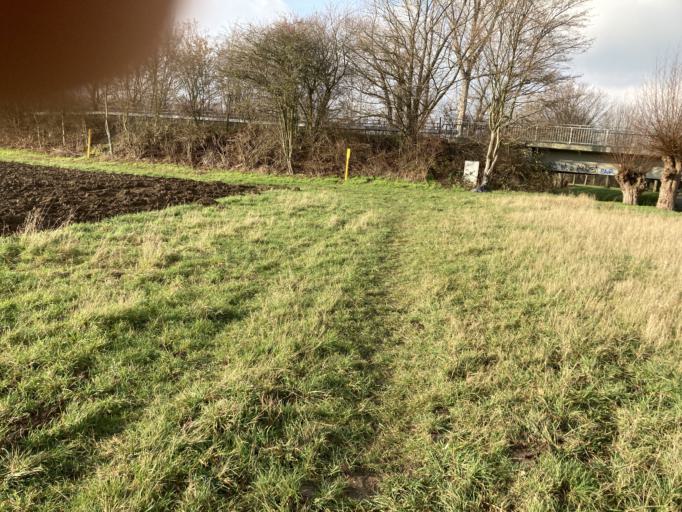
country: DE
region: North Rhine-Westphalia
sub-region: Regierungsbezirk Koln
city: Bergheim
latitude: 50.9321
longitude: 6.6706
